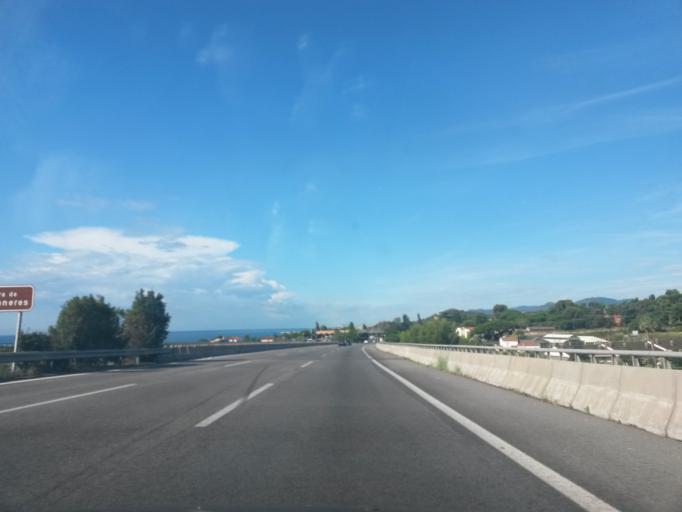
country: ES
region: Catalonia
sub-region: Provincia de Barcelona
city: Sant Andreu de Llavaneres
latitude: 41.5650
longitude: 2.4953
